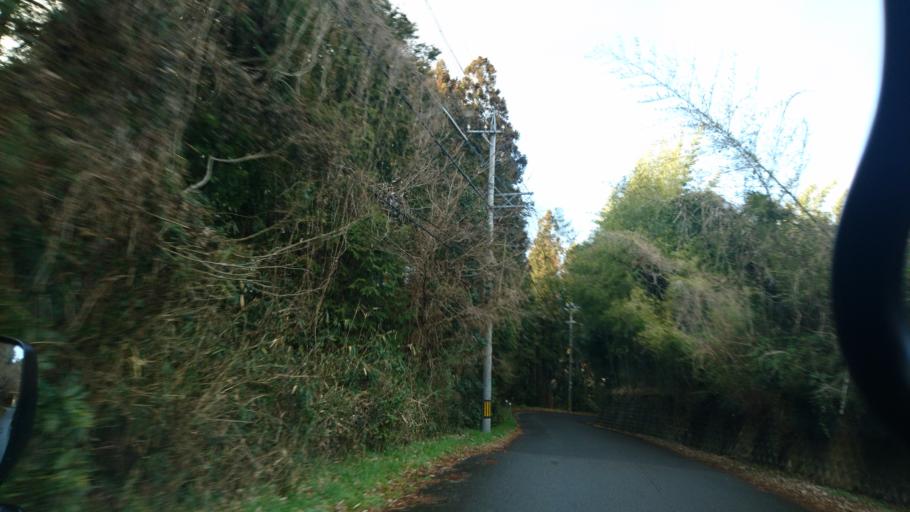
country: JP
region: Mie
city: Ueno-ebisumachi
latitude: 34.7629
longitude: 136.0563
